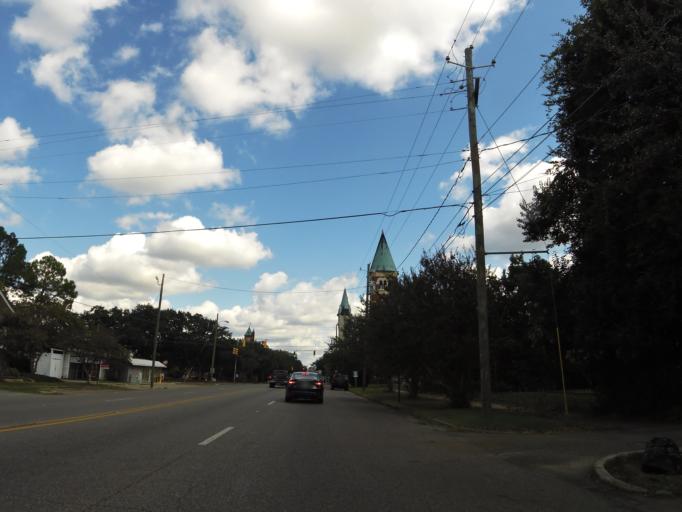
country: US
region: Alabama
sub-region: Dallas County
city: Selma
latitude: 32.4089
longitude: -87.0241
